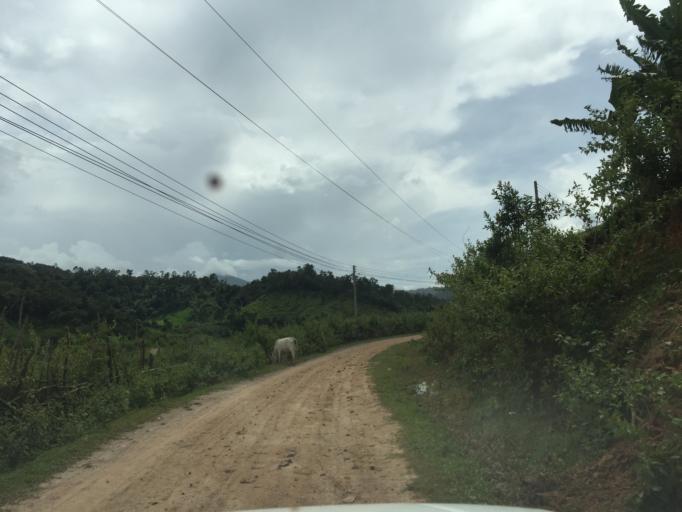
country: LA
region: Xiangkhoang
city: Muang Phonsavan
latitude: 19.3398
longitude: 103.5335
